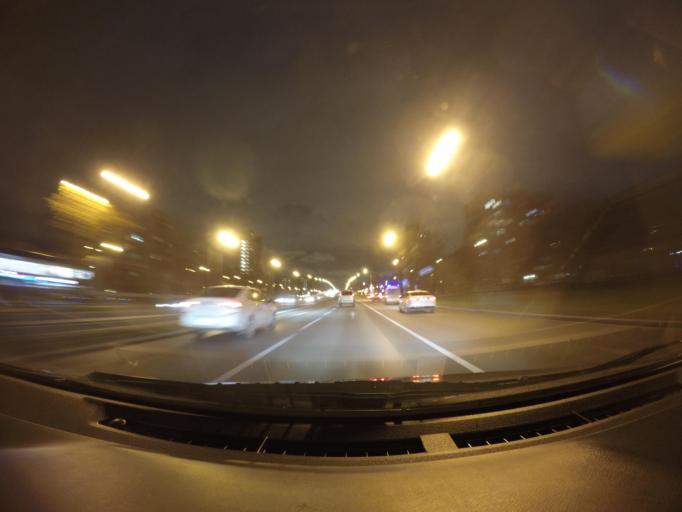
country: RU
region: Moscow
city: Novyye Kuz'minki
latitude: 55.7071
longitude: 37.7529
